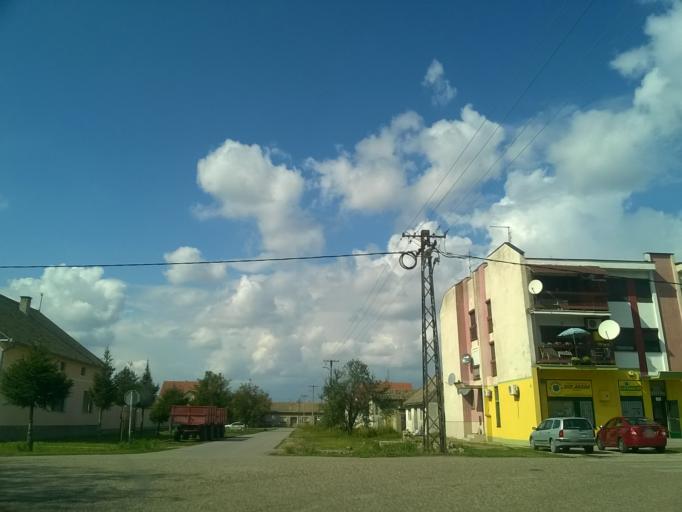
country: RS
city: Lokve
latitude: 45.1514
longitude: 21.0285
